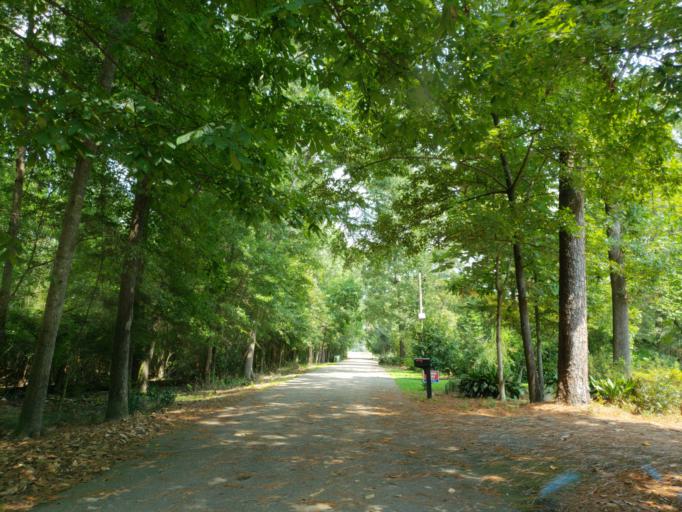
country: US
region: Mississippi
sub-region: Lamar County
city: West Hattiesburg
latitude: 31.3176
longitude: -89.3453
